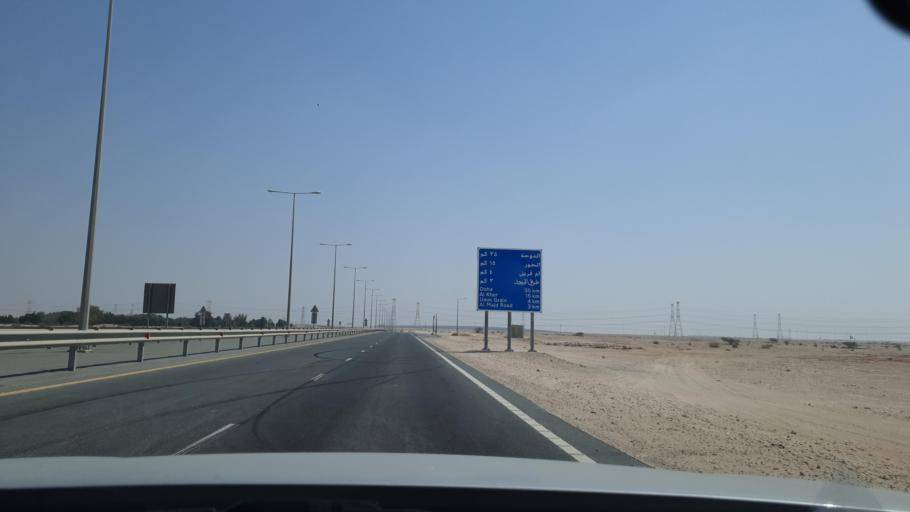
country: QA
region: Baladiyat az Za`ayin
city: Az Za`ayin
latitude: 25.6233
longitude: 51.3433
